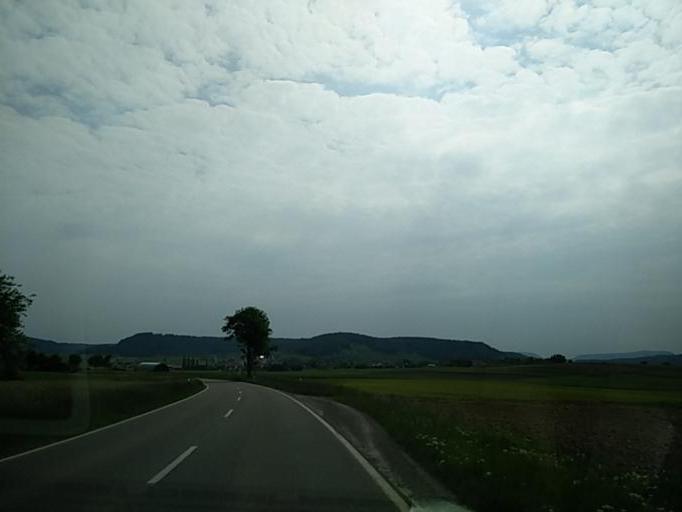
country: DE
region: Baden-Wuerttemberg
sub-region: Tuebingen Region
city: Hirrlingen
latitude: 48.4173
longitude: 8.9036
